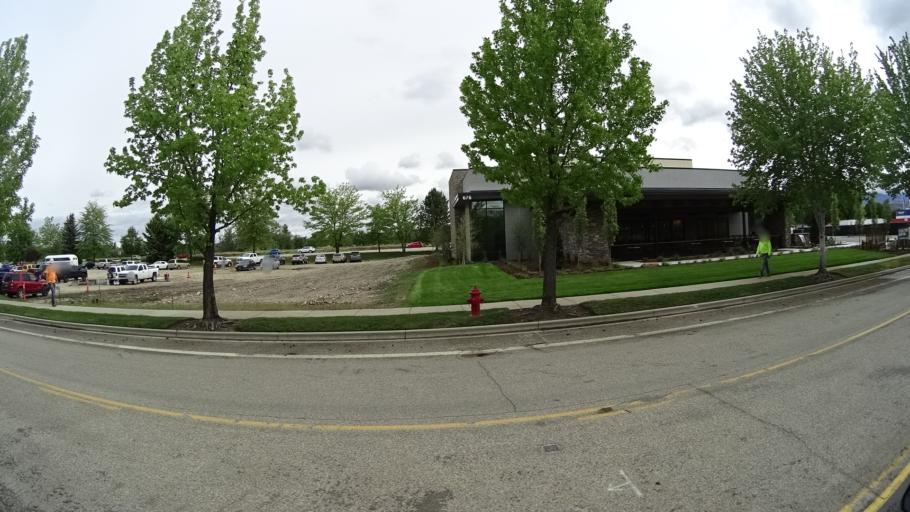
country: US
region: Idaho
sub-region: Ada County
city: Eagle
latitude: 43.6892
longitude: -116.3466
